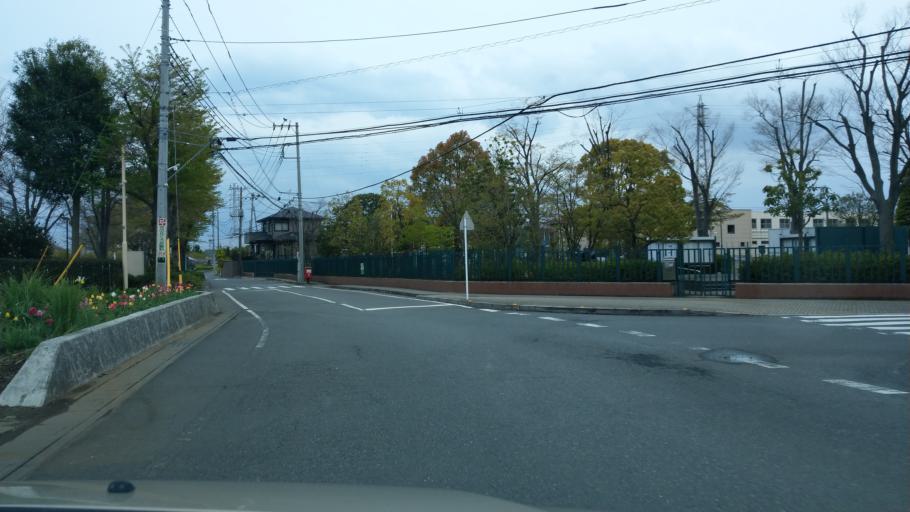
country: JP
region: Saitama
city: Ageoshimo
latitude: 35.9386
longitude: 139.5973
